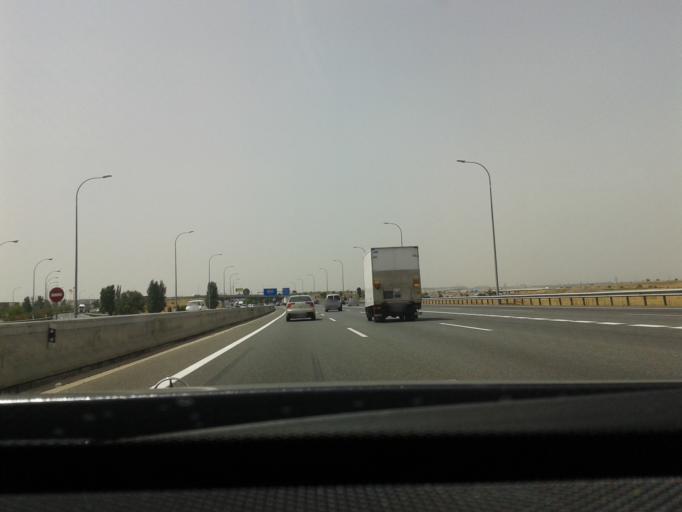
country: ES
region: Madrid
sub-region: Provincia de Madrid
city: Torrejon de Ardoz
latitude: 40.4605
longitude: -3.4986
